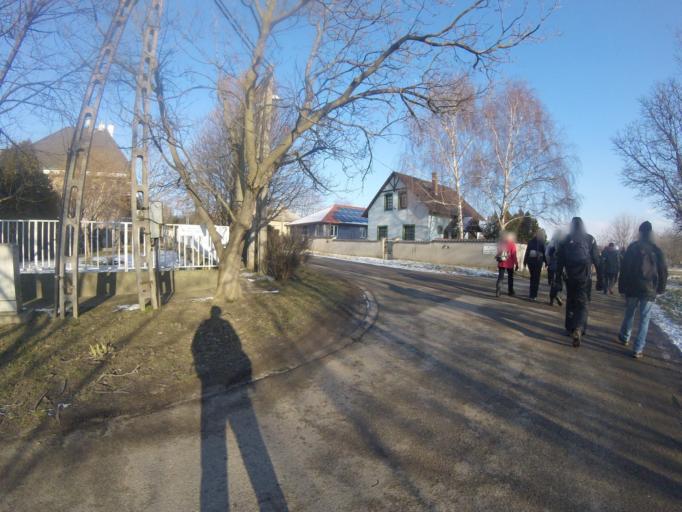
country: HU
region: Pest
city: Ecser
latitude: 47.4558
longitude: 19.2982
